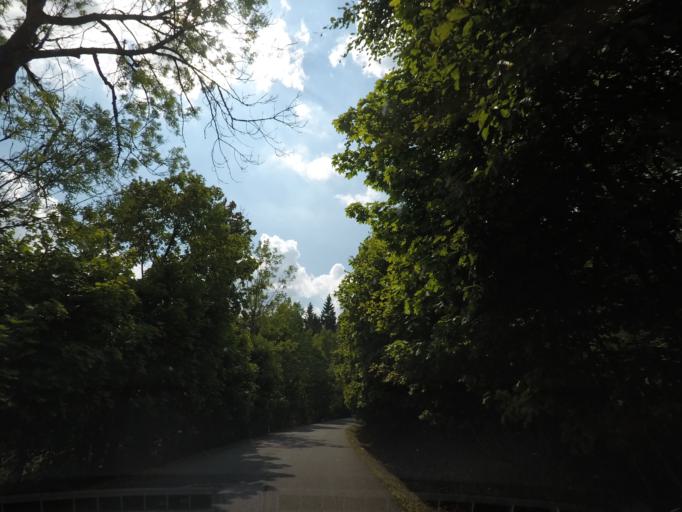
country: CZ
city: Radvanice
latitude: 50.6147
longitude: 16.0628
